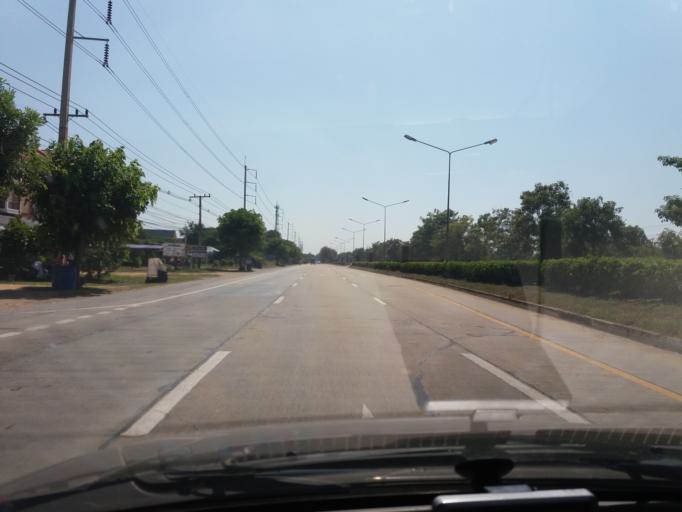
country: TH
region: Chai Nat
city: Sankhaburi
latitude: 15.0525
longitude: 100.1515
